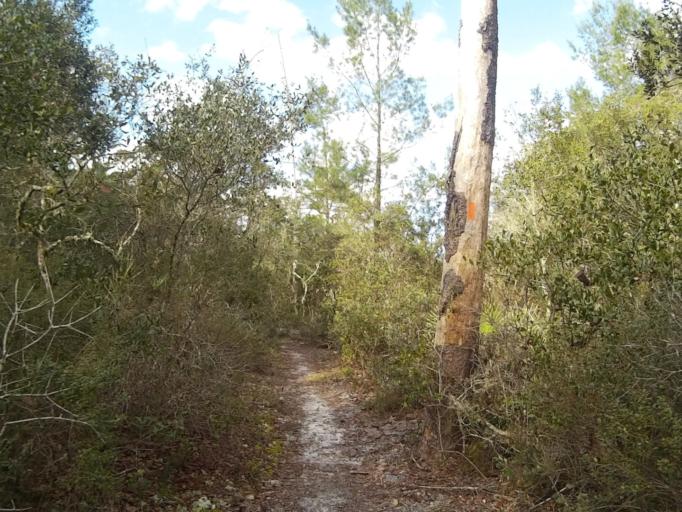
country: US
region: Florida
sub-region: Lake County
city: Astor
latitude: 29.0690
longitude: -81.6150
